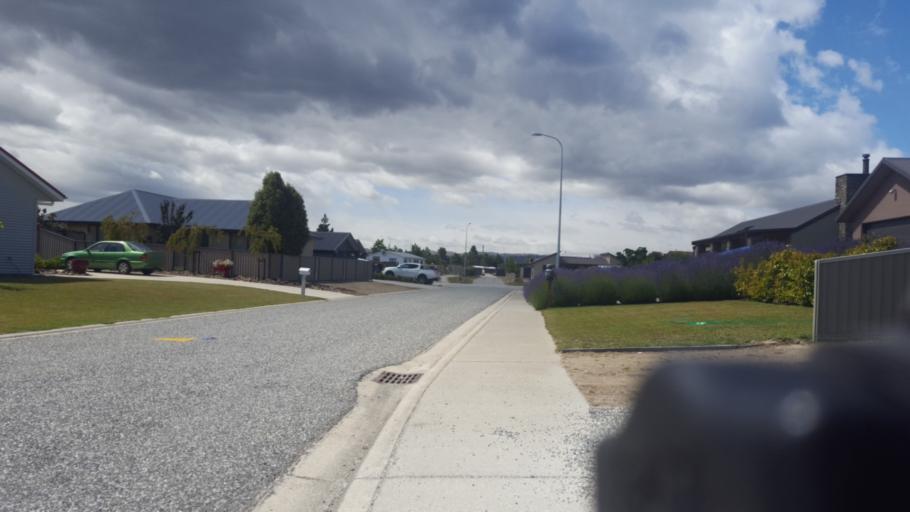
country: NZ
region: Otago
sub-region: Queenstown-Lakes District
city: Wanaka
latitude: -45.1956
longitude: 169.3341
